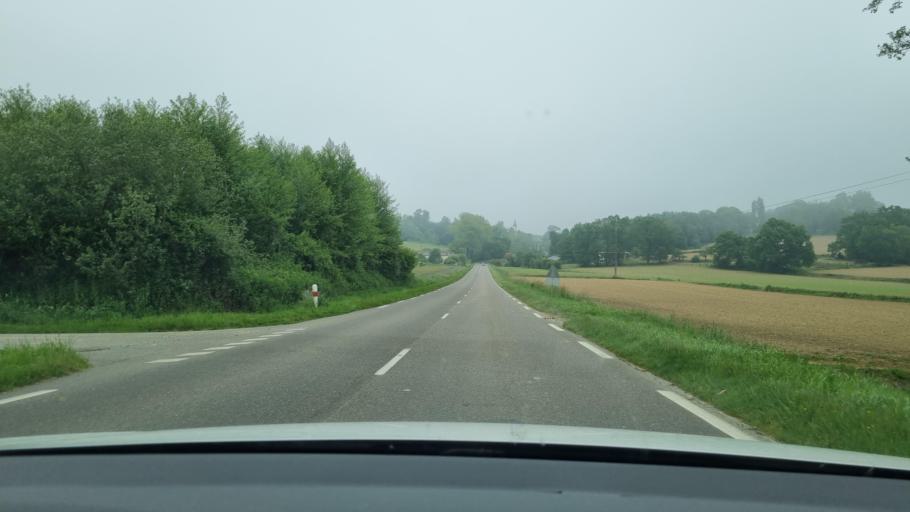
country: FR
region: Aquitaine
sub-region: Departement des Landes
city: Hagetmau
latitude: 43.6063
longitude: -0.6408
